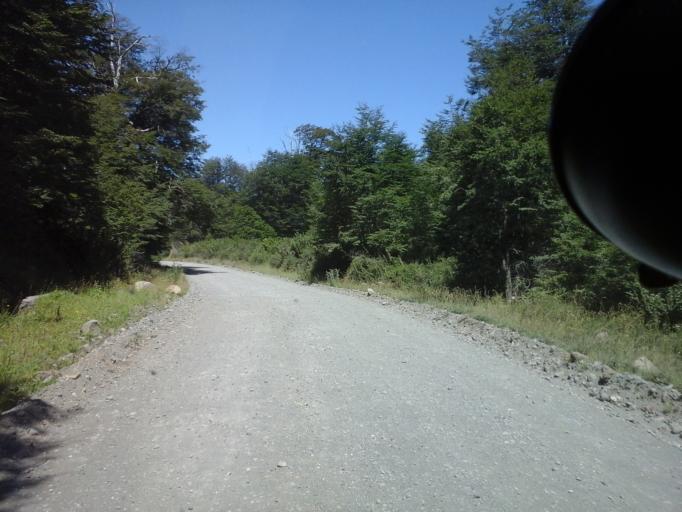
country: AR
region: Neuquen
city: Villa La Angostura
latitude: -41.2139
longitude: -71.8035
